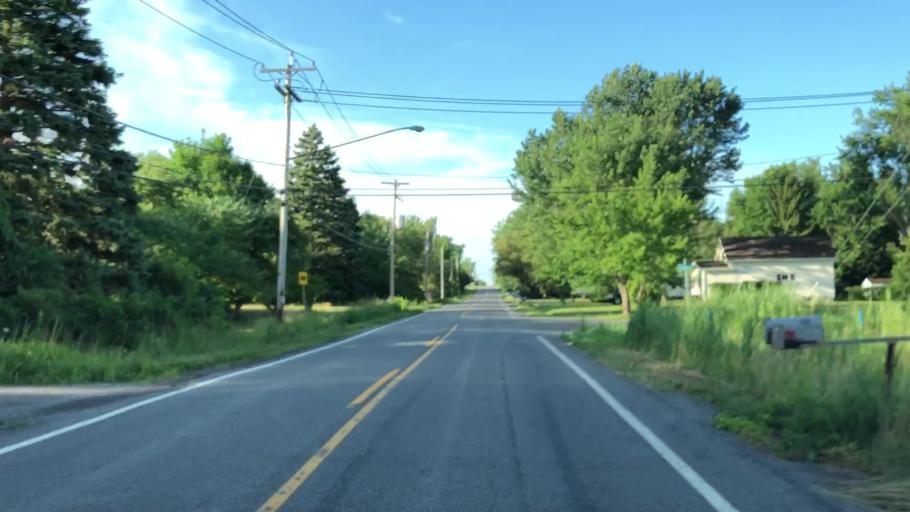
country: US
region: New York
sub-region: Erie County
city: Depew
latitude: 42.8465
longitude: -78.6923
